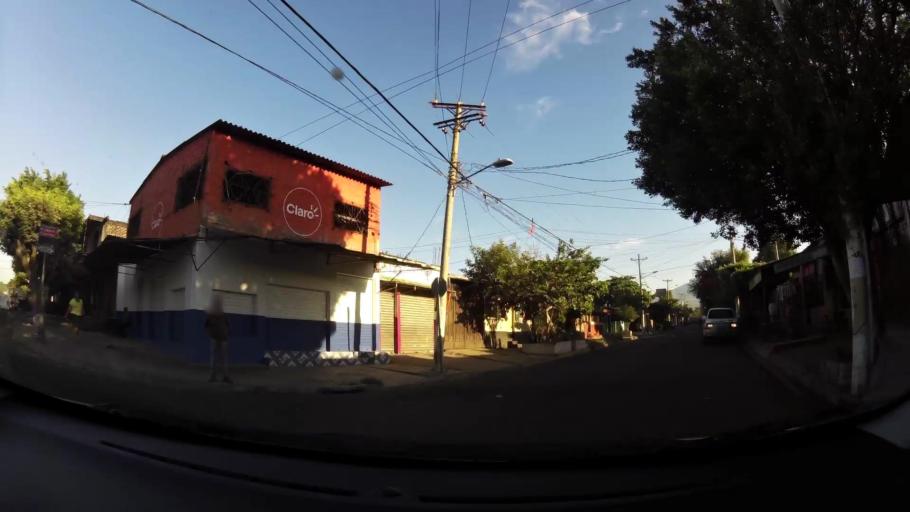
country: SV
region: Sonsonate
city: San Antonio del Monte
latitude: 13.7111
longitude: -89.7302
